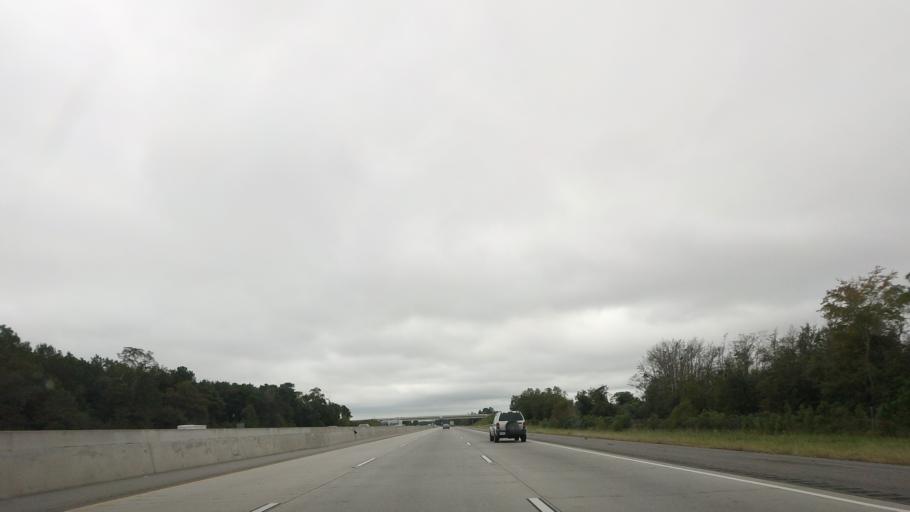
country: US
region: Georgia
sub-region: Tift County
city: Omega
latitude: 31.2969
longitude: -83.4774
